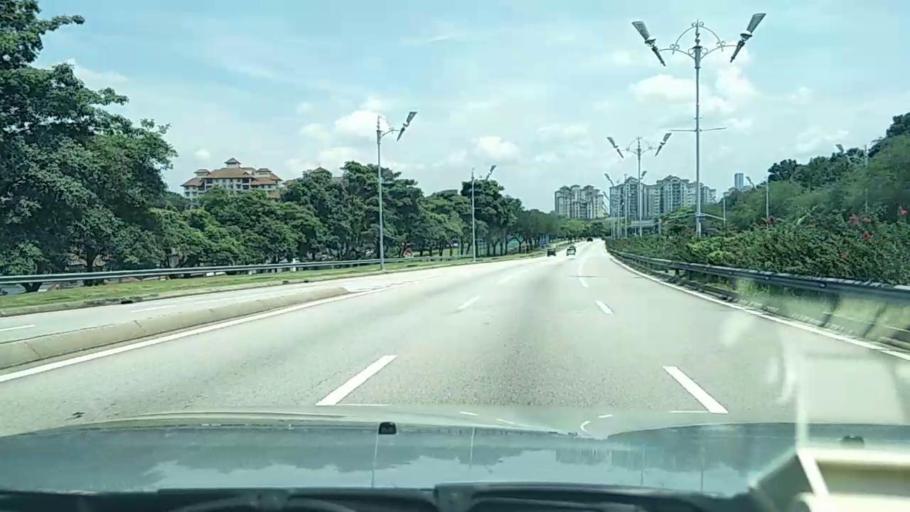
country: MY
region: Putrajaya
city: Putrajaya
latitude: 2.9495
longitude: 101.6822
